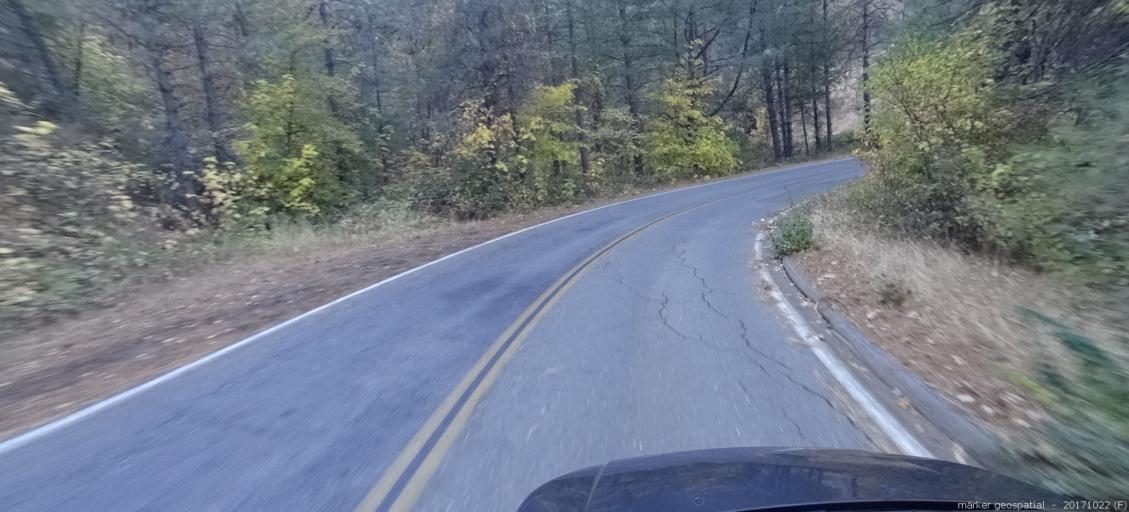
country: US
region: California
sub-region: Shasta County
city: Shasta Lake
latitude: 40.9155
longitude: -122.2463
